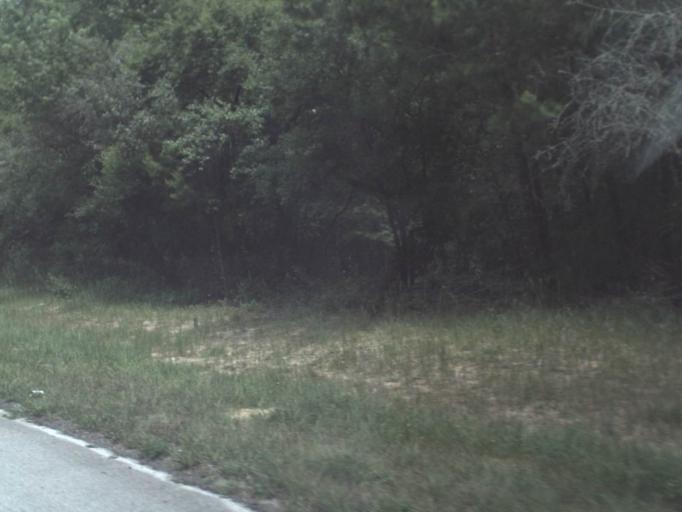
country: US
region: Florida
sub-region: Putnam County
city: Palatka
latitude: 29.5263
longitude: -81.6384
